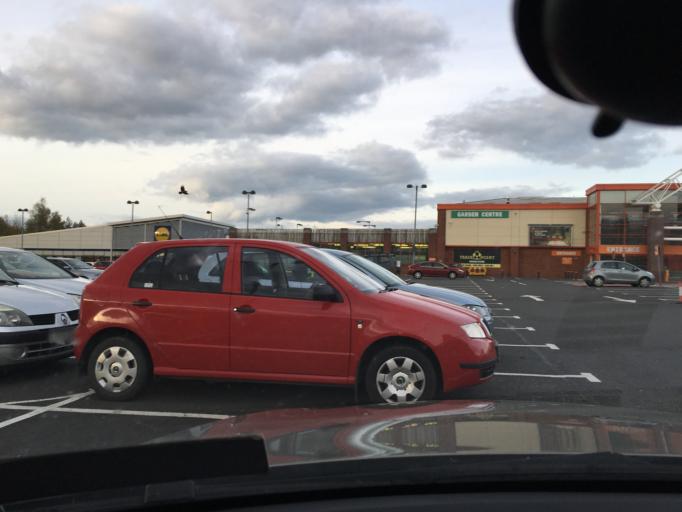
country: GB
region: Northern Ireland
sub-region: Newry and Mourne District
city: Newry
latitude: 54.1919
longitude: -6.3504
